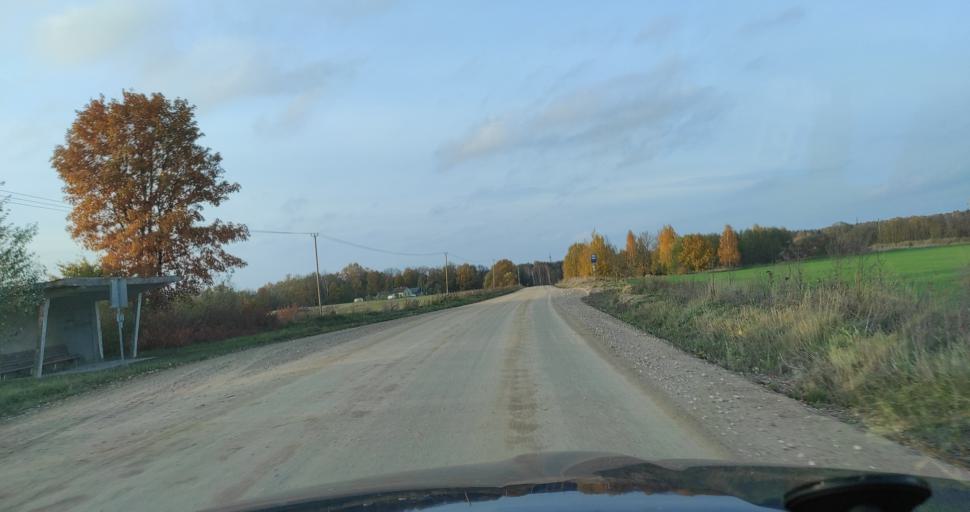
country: LV
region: Vainode
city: Vainode
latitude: 56.4424
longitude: 21.8735
